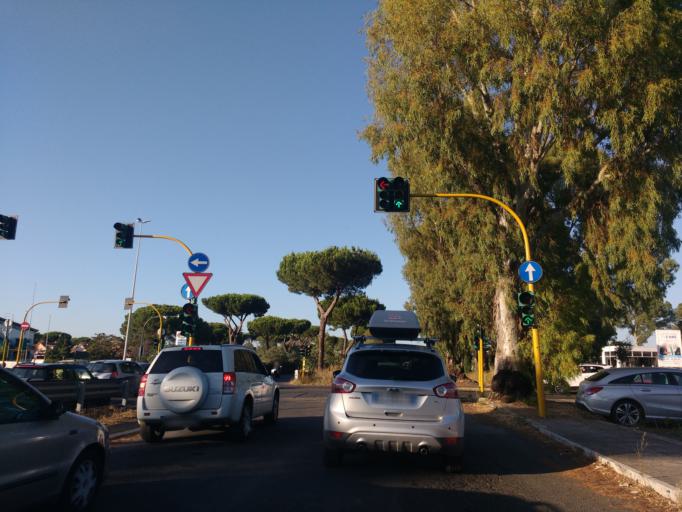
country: IT
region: Latium
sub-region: Citta metropolitana di Roma Capitale
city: Acilia-Castel Fusano-Ostia Antica
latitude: 41.7546
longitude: 12.3697
